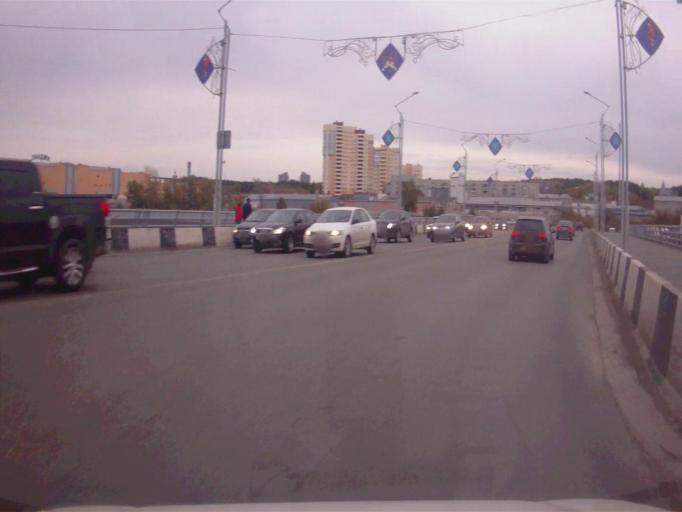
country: RU
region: Chelyabinsk
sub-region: Gorod Chelyabinsk
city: Chelyabinsk
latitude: 55.1738
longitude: 61.3479
